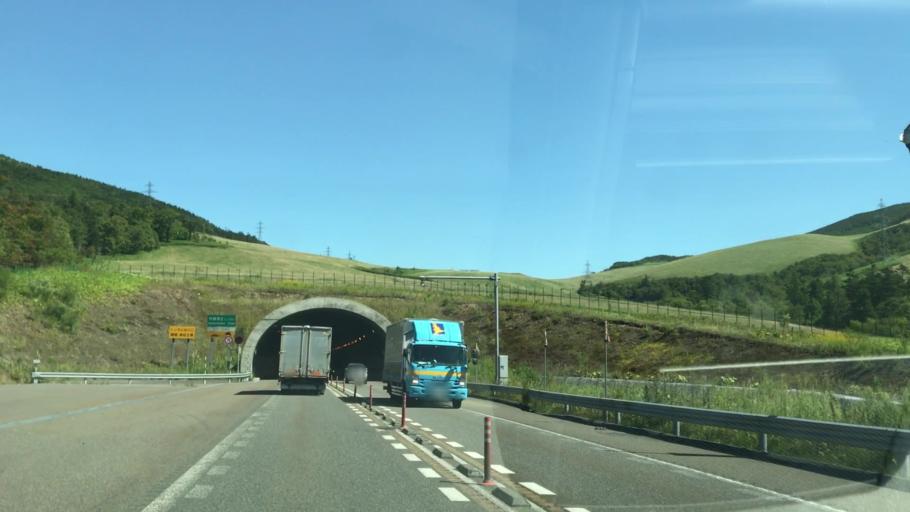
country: JP
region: Hokkaido
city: Shimo-furano
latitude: 43.0612
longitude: 142.7176
